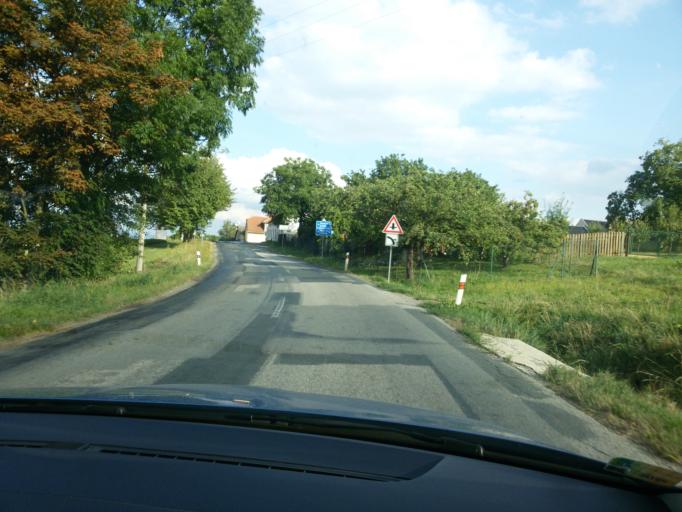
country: CZ
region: South Moravian
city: Olesnice
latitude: 49.5284
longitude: 16.4626
